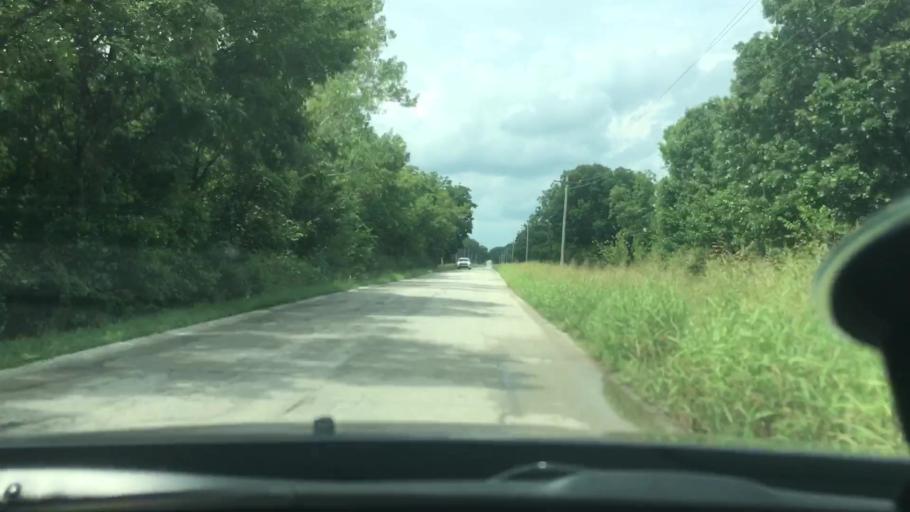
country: US
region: Oklahoma
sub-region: Carter County
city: Dickson
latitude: 34.2527
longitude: -96.9425
